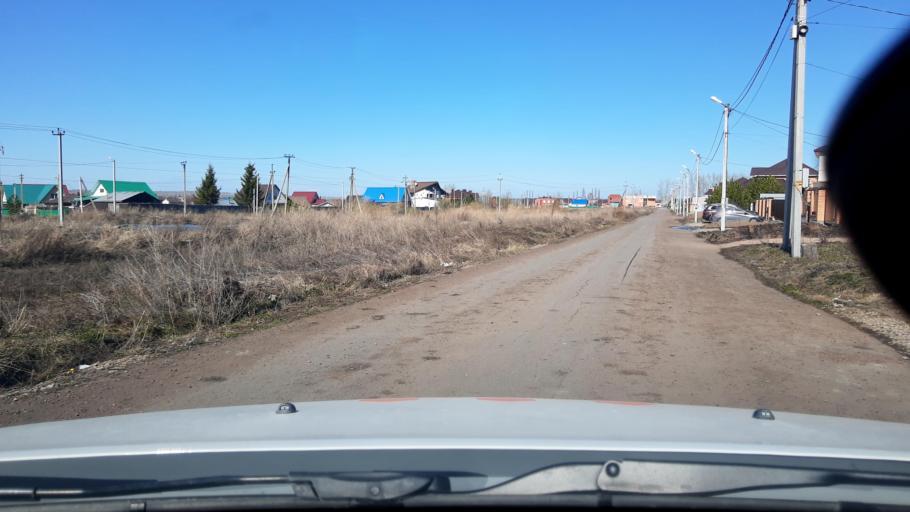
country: RU
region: Bashkortostan
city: Kabakovo
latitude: 54.6165
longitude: 56.1141
